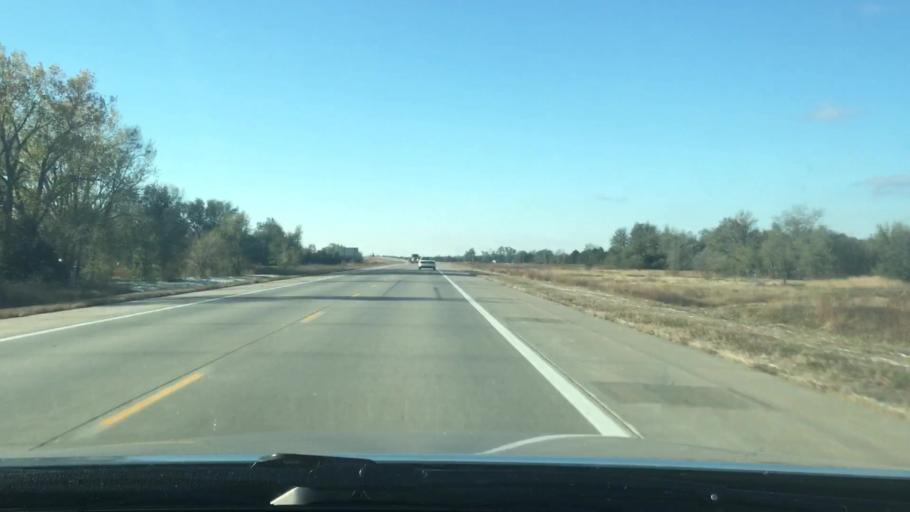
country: US
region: Kansas
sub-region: Reno County
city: Hutchinson
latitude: 38.0972
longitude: -98.0056
